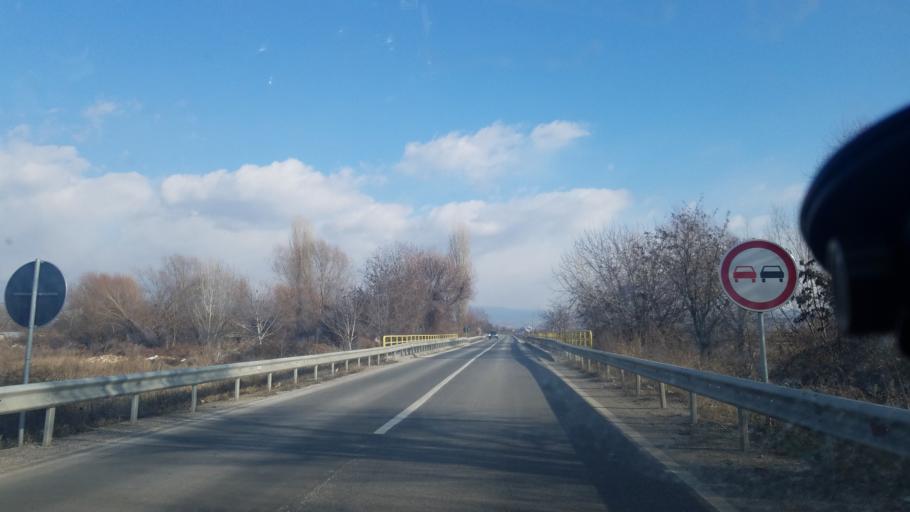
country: MK
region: Kocani
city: Kochani
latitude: 41.9020
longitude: 22.4024
